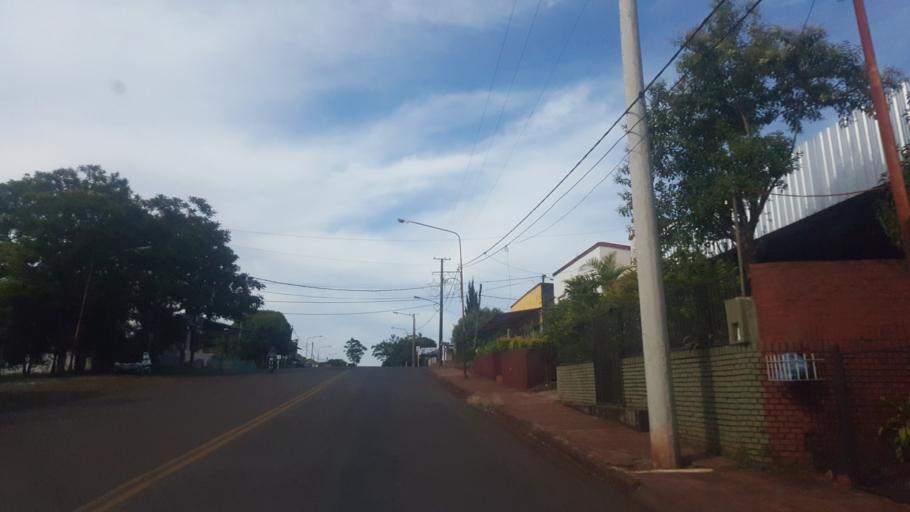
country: AR
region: Misiones
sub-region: Departamento de Leandro N. Alem
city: Leandro N. Alem
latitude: -27.5966
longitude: -55.3240
